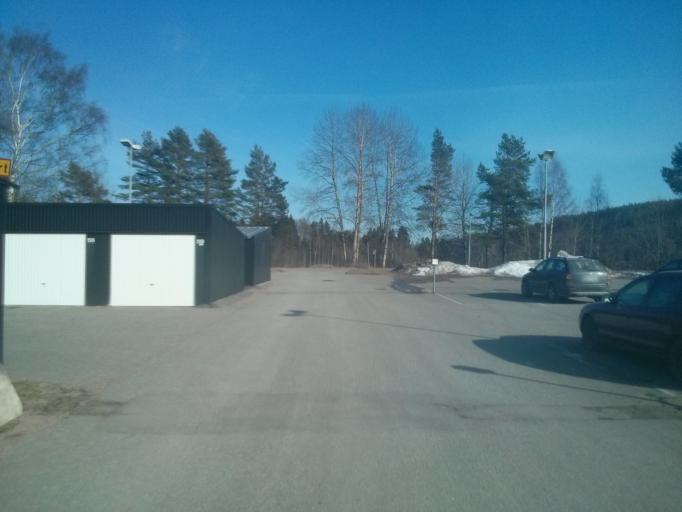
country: SE
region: Vaesternorrland
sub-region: Sundsvalls Kommun
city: Skottsund
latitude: 62.2972
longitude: 17.3827
